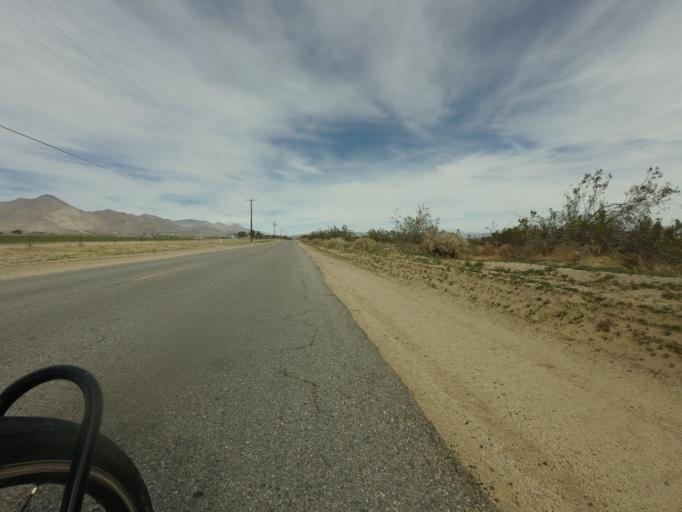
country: US
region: California
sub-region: Kern County
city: Inyokern
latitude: 35.7420
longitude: -117.8406
